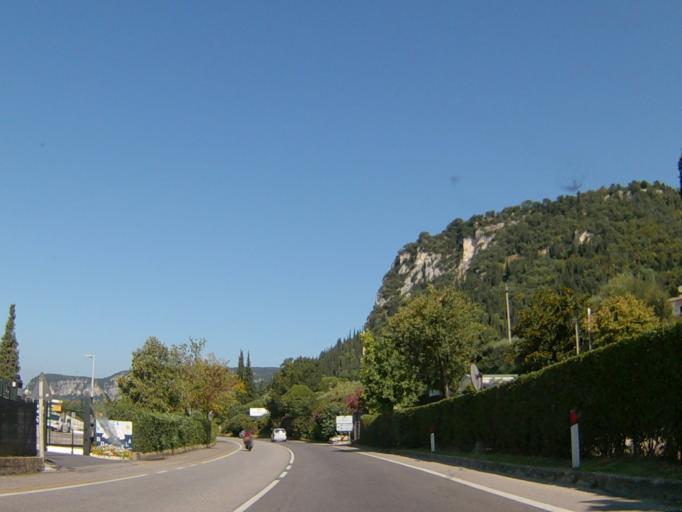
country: IT
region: Veneto
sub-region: Provincia di Verona
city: Garda
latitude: 45.5638
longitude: 10.7140
